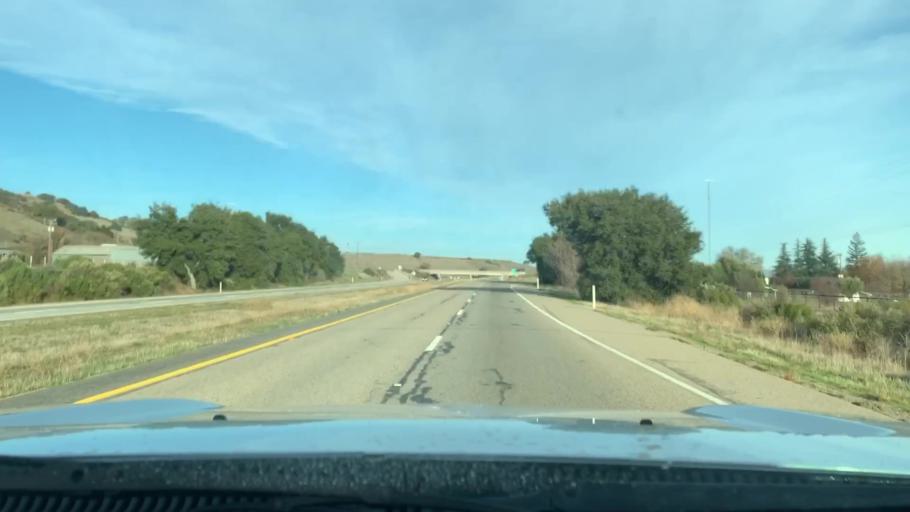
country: US
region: California
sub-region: San Luis Obispo County
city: Lake Nacimiento
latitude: 35.9721
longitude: -120.8969
